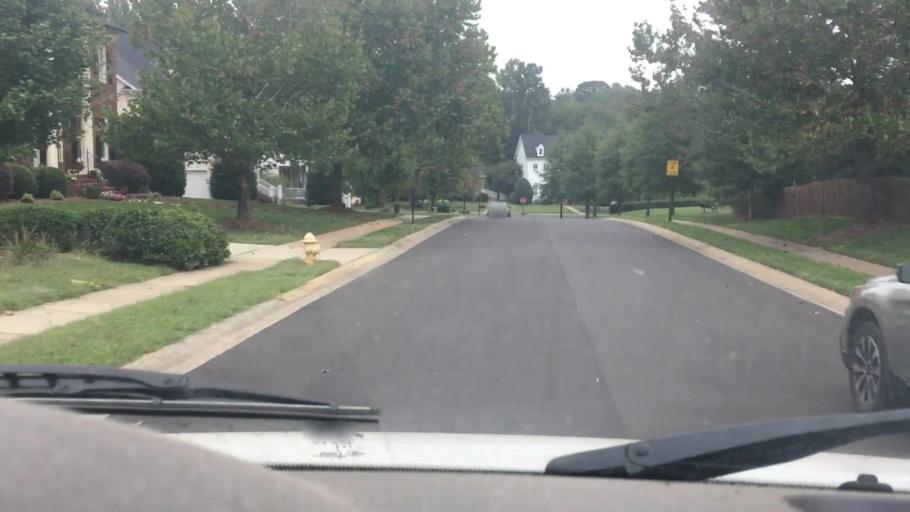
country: US
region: North Carolina
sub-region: Gaston County
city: Davidson
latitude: 35.4928
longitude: -80.8298
